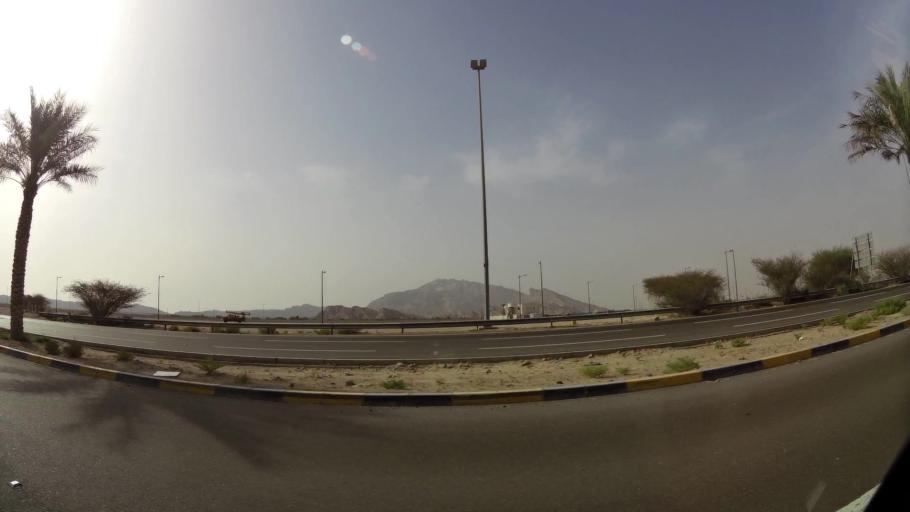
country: AE
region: Abu Dhabi
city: Al Ain
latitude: 24.1332
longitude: 55.7332
